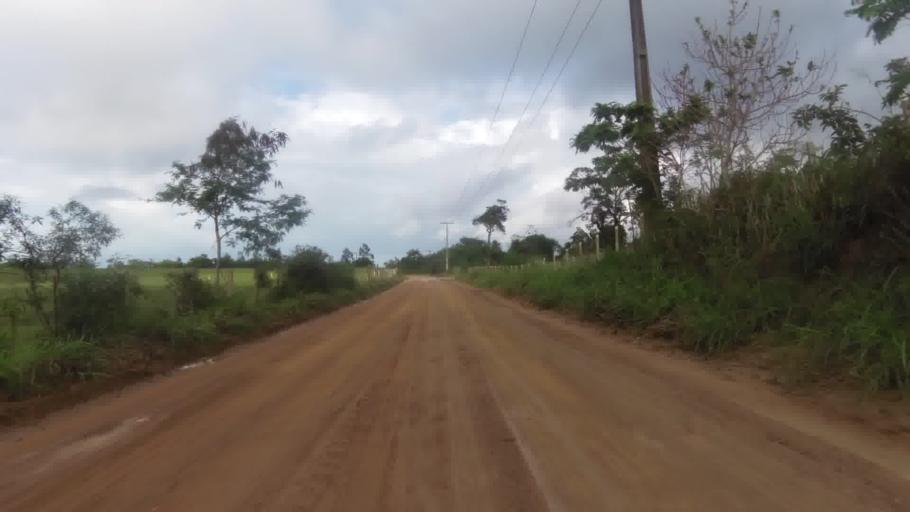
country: BR
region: Espirito Santo
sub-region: Piuma
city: Piuma
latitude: -20.7799
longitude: -40.6304
